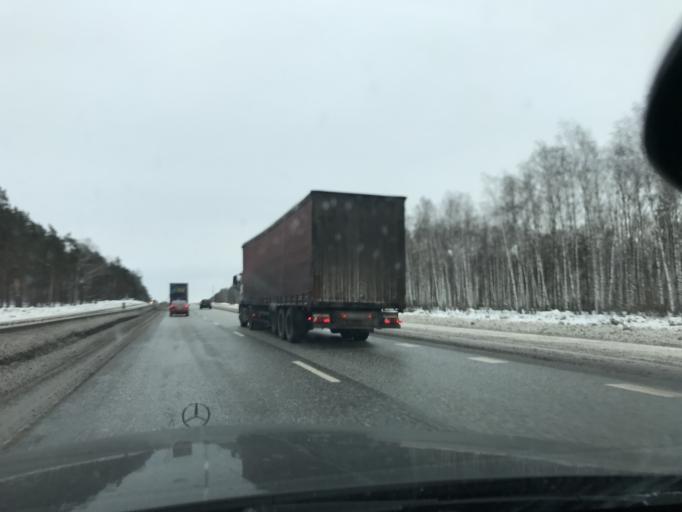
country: RU
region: Nizjnij Novgorod
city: Novosmolinskiy
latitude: 56.2788
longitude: 43.0295
